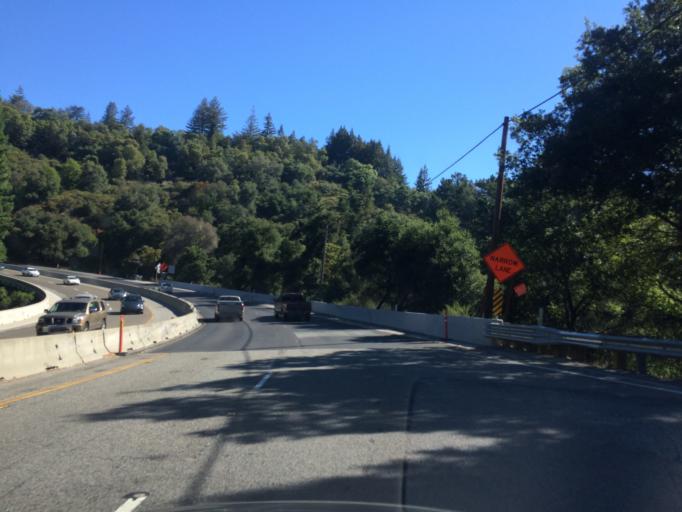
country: US
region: California
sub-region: Santa Clara County
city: Lexington Hills
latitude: 37.1043
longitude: -121.9750
